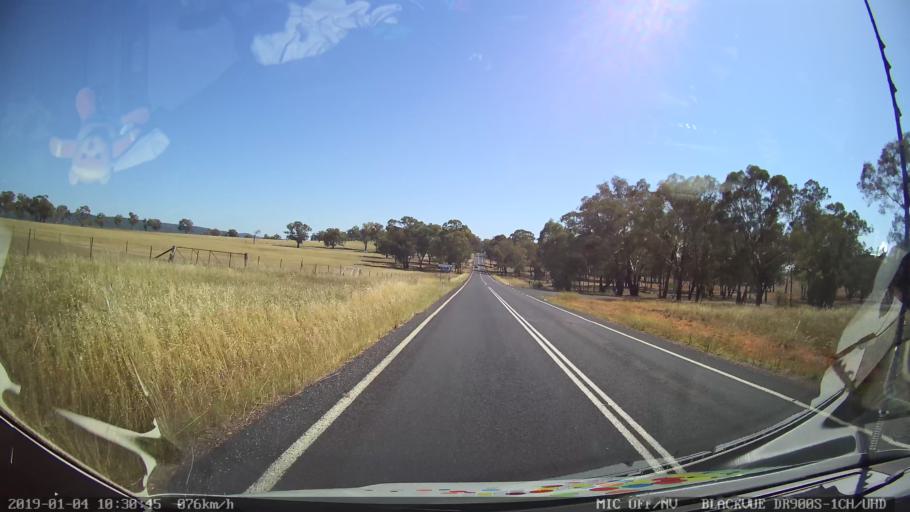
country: AU
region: New South Wales
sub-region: Cabonne
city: Canowindra
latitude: -33.3424
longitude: 148.6294
